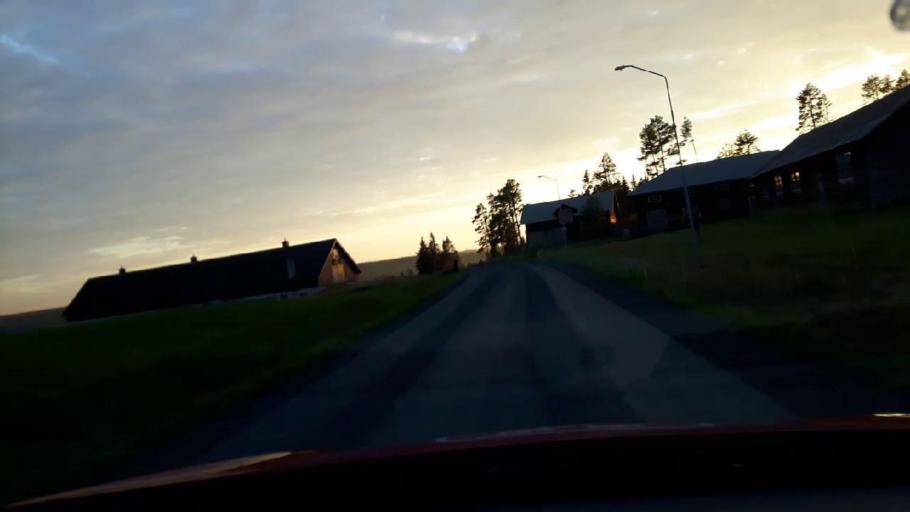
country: SE
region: Jaemtland
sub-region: OEstersunds Kommun
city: Lit
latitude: 63.2864
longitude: 14.7857
